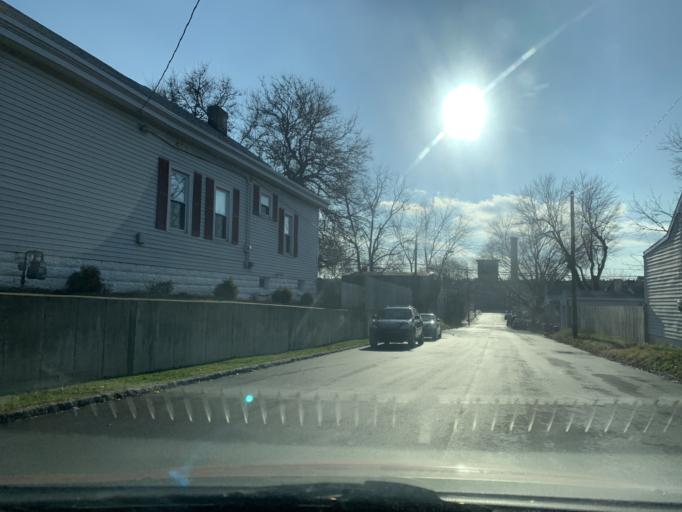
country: US
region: Kentucky
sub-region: Jefferson County
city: Audubon Park
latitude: 38.2312
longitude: -85.7376
